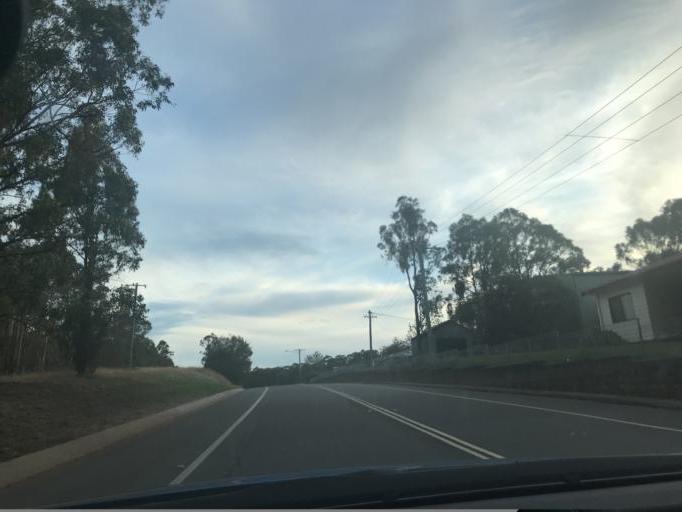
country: AU
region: New South Wales
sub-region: Cessnock
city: Cessnock
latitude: -32.8637
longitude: 151.3170
